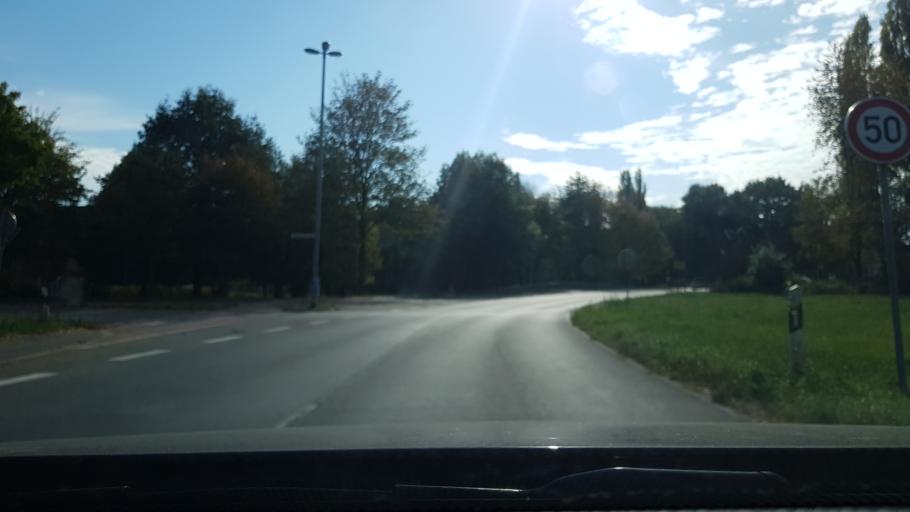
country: DE
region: North Rhine-Westphalia
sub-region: Regierungsbezirk Dusseldorf
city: Moers
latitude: 51.4204
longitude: 6.6035
